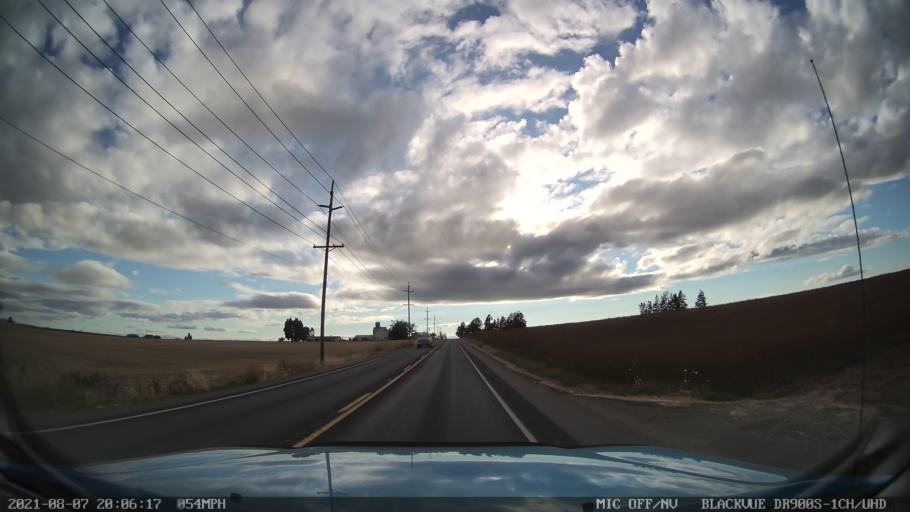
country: US
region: Oregon
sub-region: Marion County
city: Silverton
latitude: 44.9914
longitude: -122.8655
